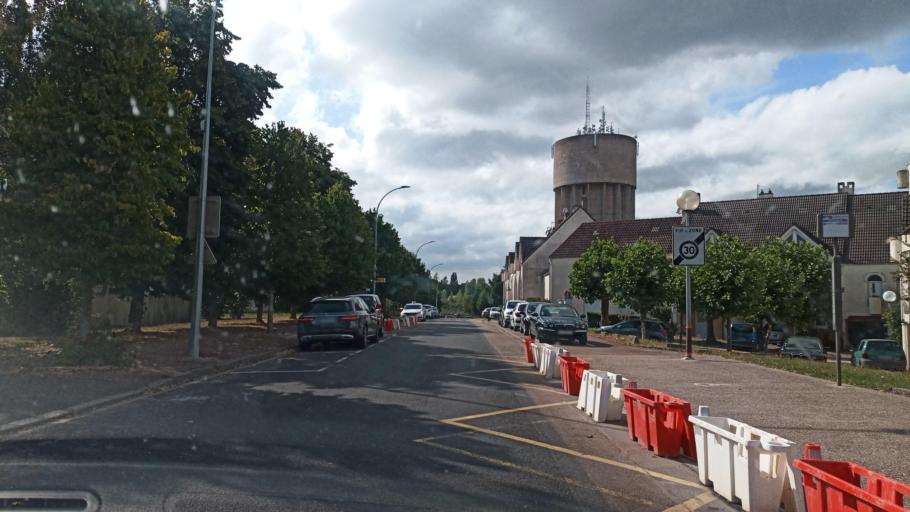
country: FR
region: Bourgogne
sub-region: Departement de l'Yonne
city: Paron
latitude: 48.1900
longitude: 3.2535
